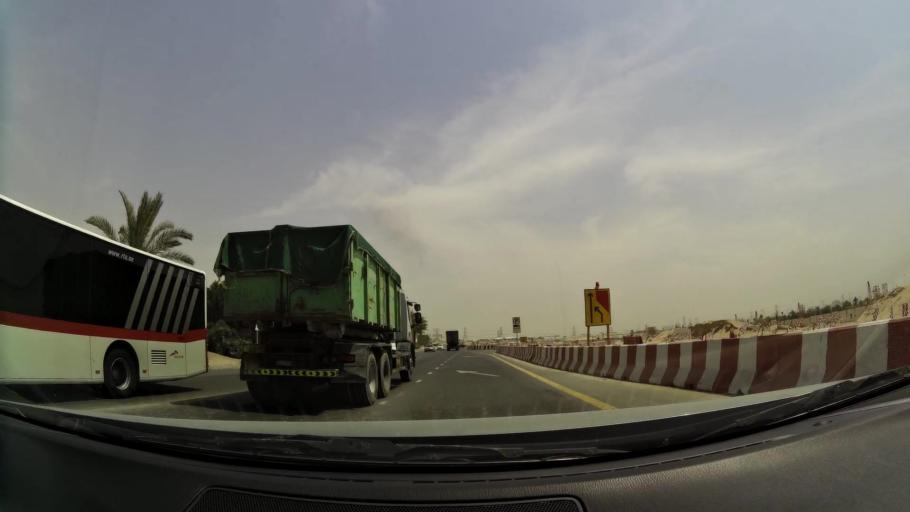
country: AE
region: Ash Shariqah
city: Sharjah
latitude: 25.1584
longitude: 55.4244
